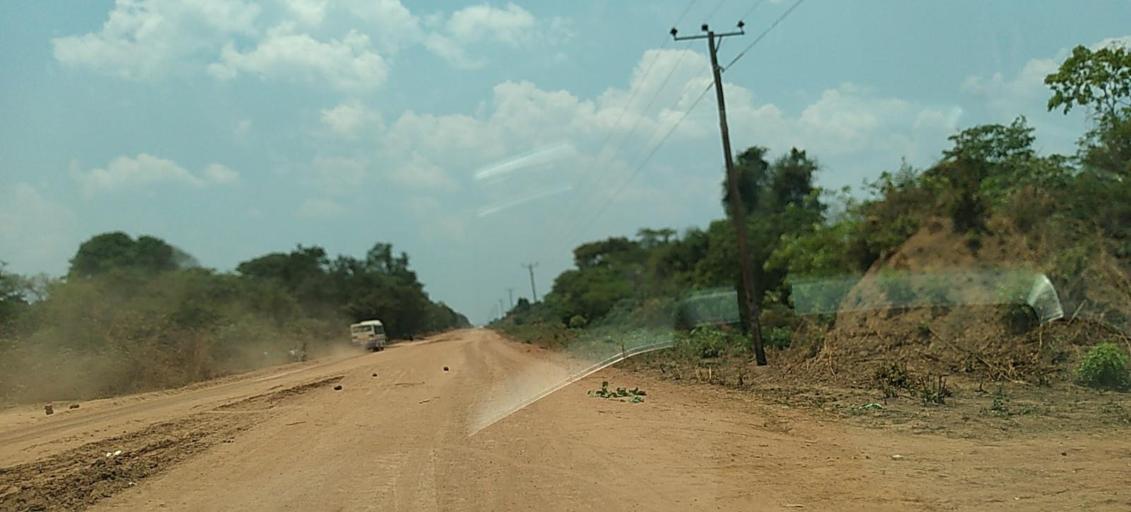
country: ZM
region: Copperbelt
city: Chingola
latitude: -12.9012
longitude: 27.5722
